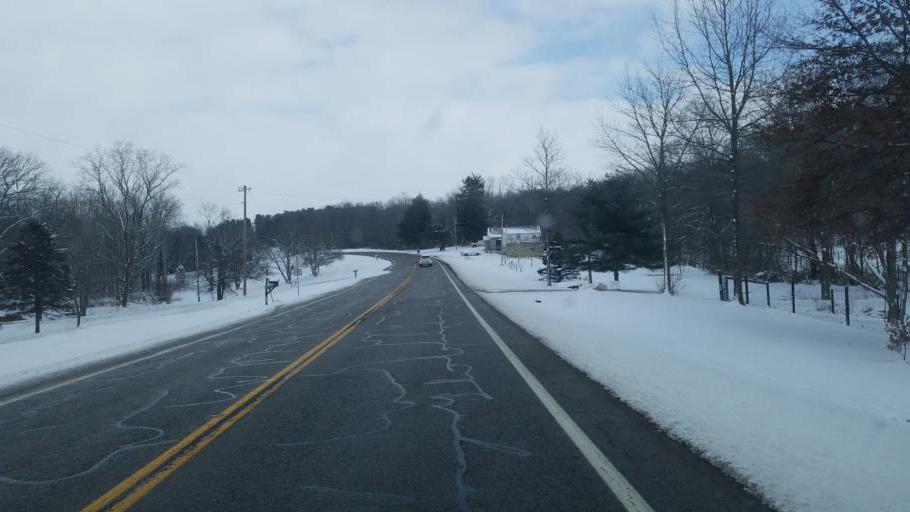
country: US
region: Ohio
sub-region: Knox County
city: Gambier
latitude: 40.4552
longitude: -82.4206
